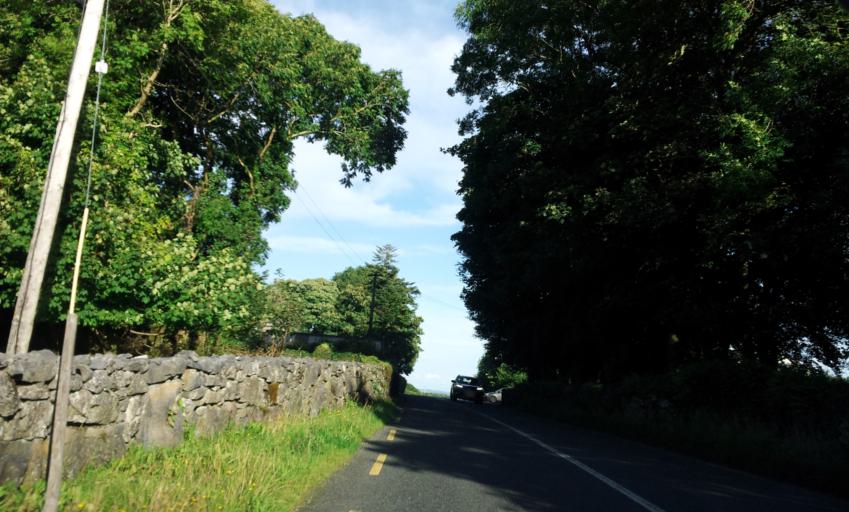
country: IE
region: Munster
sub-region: An Clar
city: Ennis
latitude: 52.9736
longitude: -9.0958
